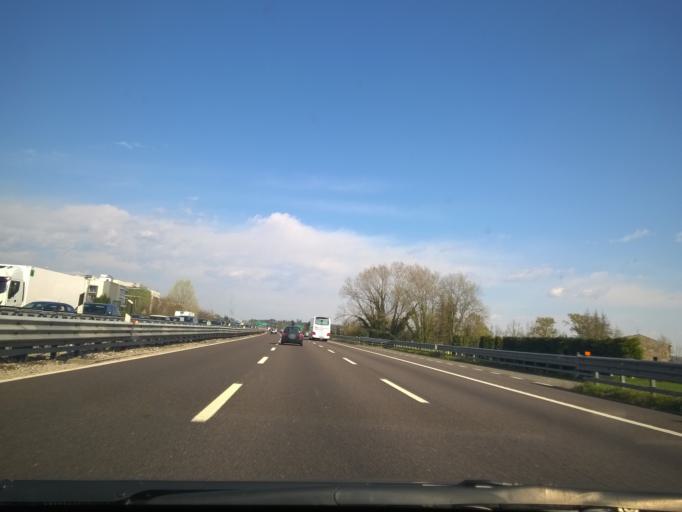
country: IT
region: Veneto
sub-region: Provincia di Verona
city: Peschiera del Garda
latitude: 45.4293
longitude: 10.6874
